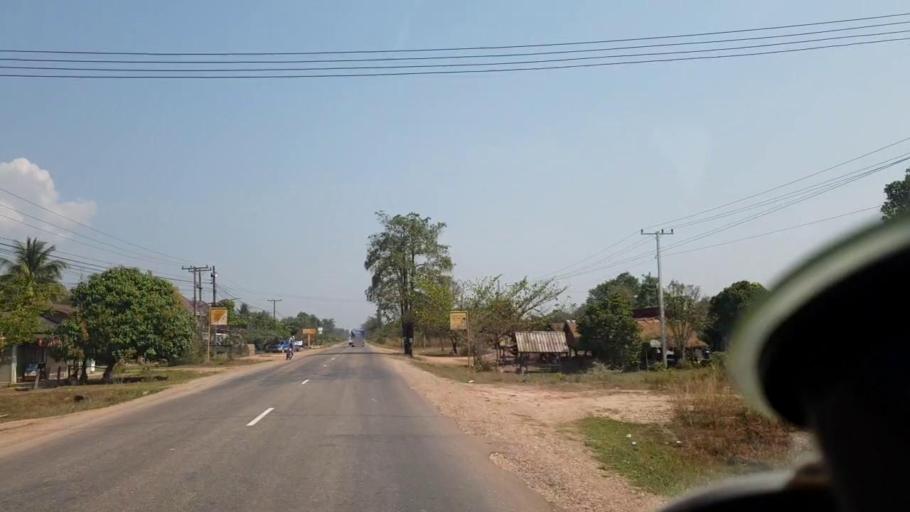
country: TH
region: Nong Khai
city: Phon Phisai
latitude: 18.1404
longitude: 103.0493
